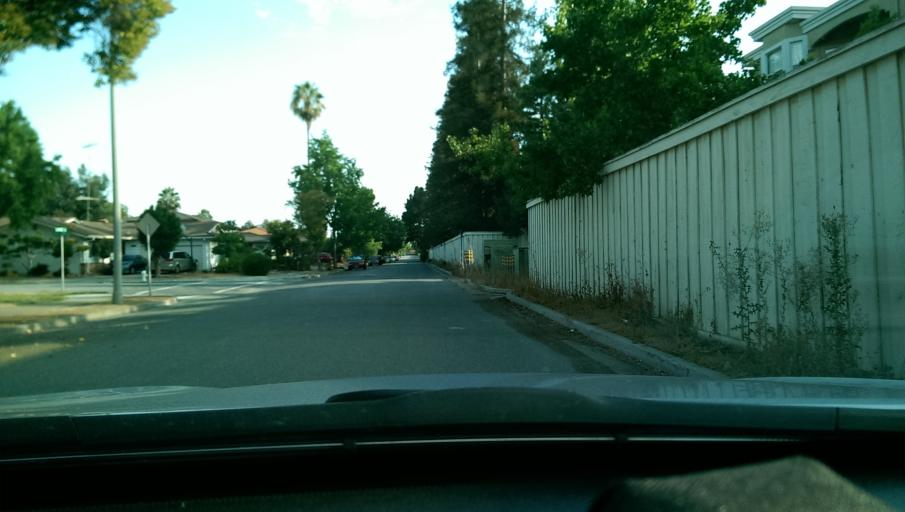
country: US
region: California
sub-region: Santa Clara County
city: Cupertino
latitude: 37.3330
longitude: -122.0164
